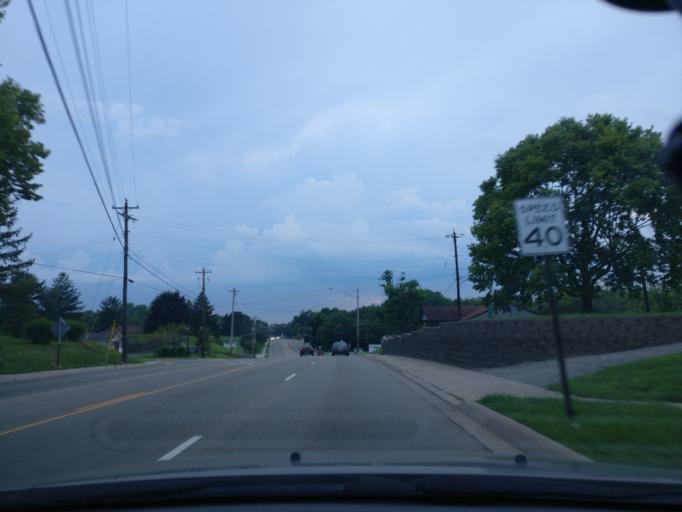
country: US
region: Ohio
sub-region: Warren County
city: Franklin
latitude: 39.5636
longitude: -84.2901
